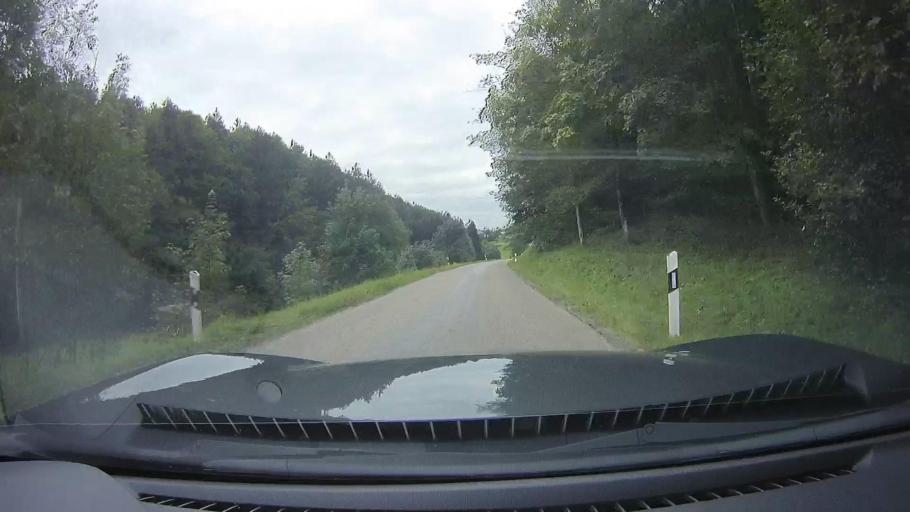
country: DE
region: Baden-Wuerttemberg
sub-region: Regierungsbezirk Stuttgart
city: Mainhardt
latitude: 49.0326
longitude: 9.5730
